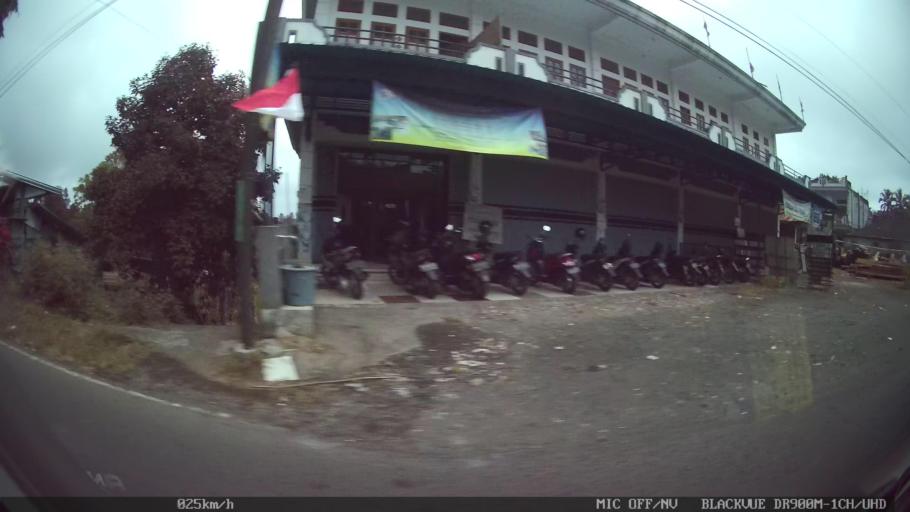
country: ID
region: Bali
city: Klau
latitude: -8.3306
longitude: 115.0325
